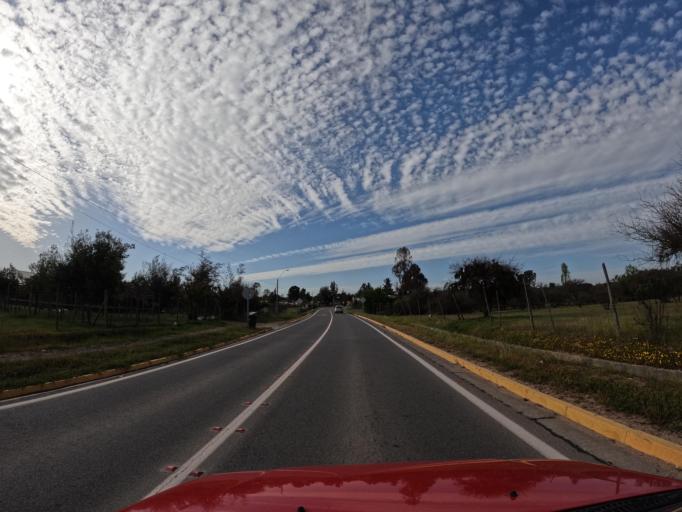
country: CL
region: O'Higgins
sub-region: Provincia de Colchagua
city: Santa Cruz
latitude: -34.2445
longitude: -71.7271
